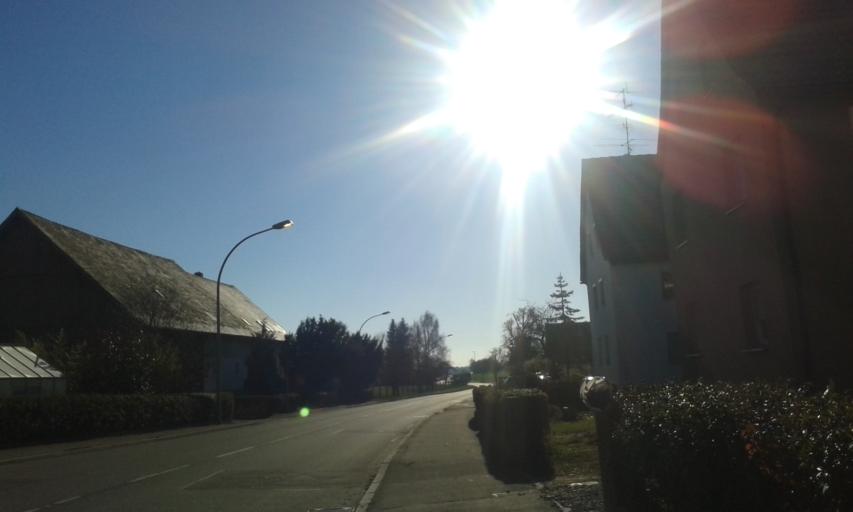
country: DE
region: Baden-Wuerttemberg
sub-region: Tuebingen Region
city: Beimerstetten
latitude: 48.4418
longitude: 9.9868
